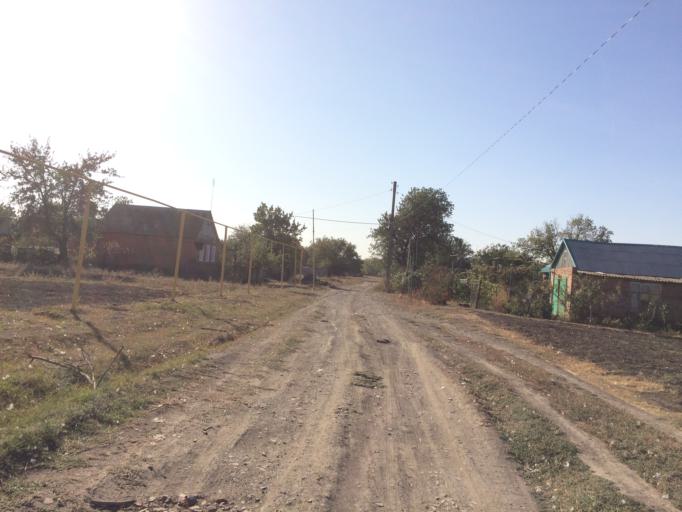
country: RU
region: Rostov
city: Gigant
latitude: 46.5219
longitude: 41.1903
